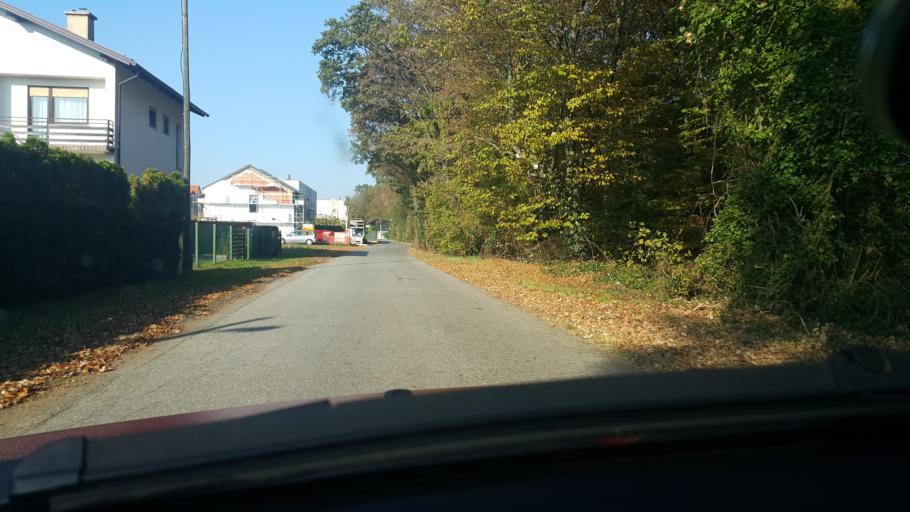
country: SI
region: Maribor
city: Maribor
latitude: 46.5367
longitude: 15.6657
